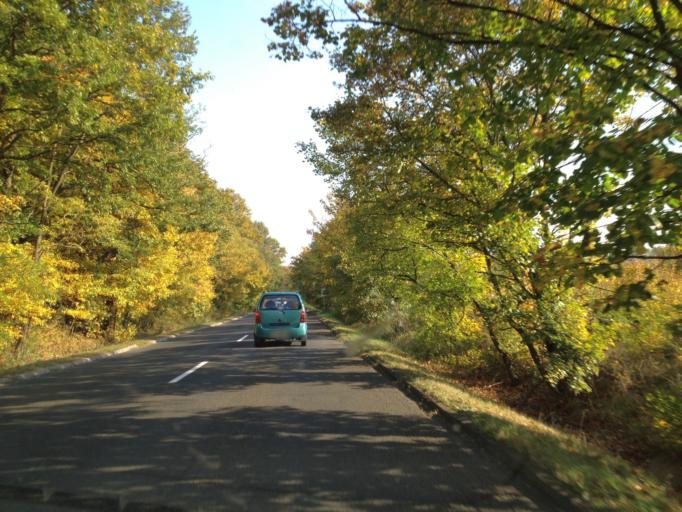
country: HU
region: Pest
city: Pilisszentkereszt
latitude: 47.6829
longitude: 18.9316
